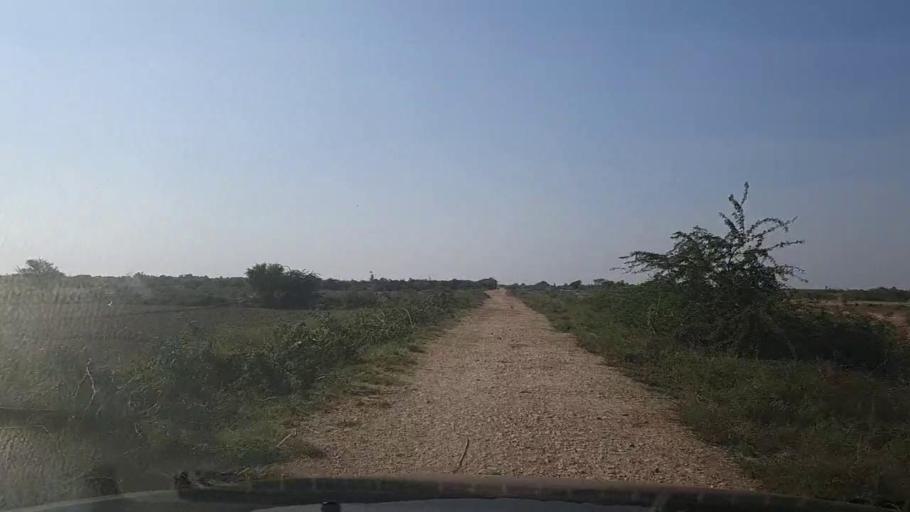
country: PK
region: Sindh
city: Gharo
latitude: 24.7113
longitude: 67.7493
